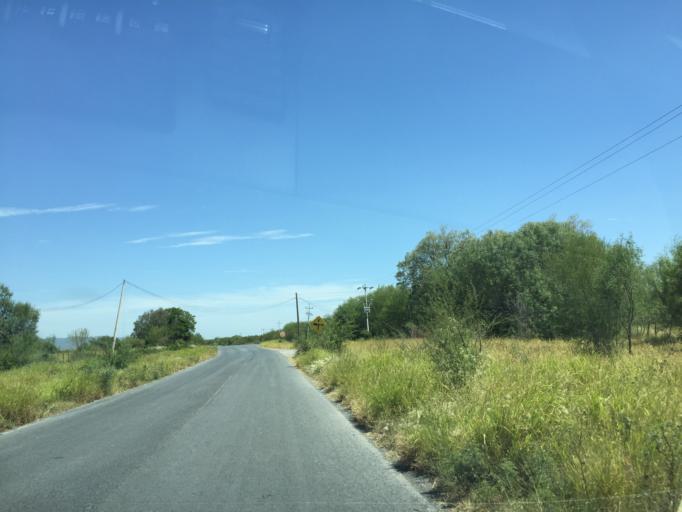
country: MX
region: Nuevo Leon
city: Marin
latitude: 25.8238
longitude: -99.8957
